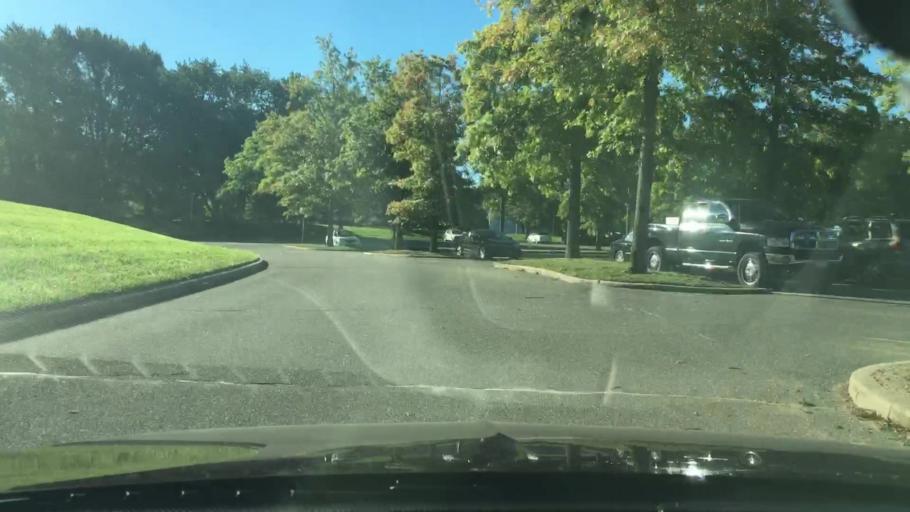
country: US
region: New York
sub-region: Suffolk County
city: Melville
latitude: 40.7781
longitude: -73.4061
